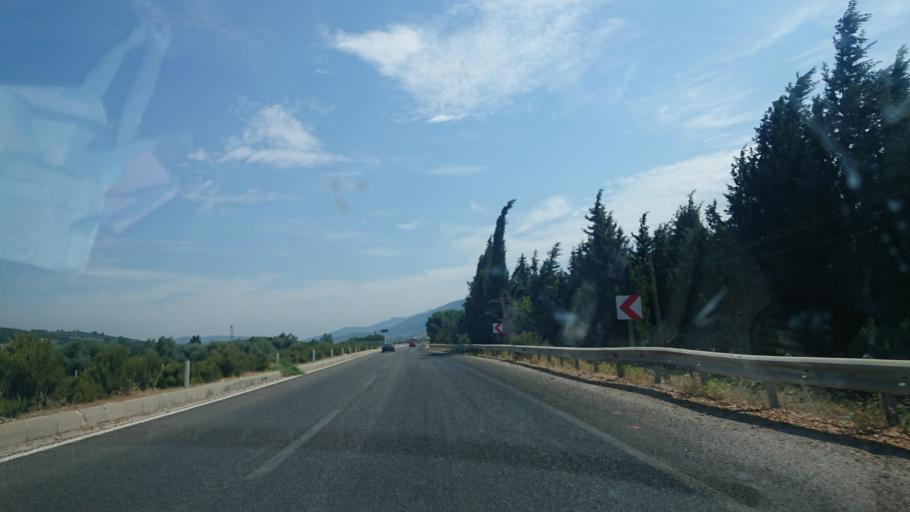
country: TR
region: Izmir
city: Dagkizilca
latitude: 38.2501
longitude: 27.3820
